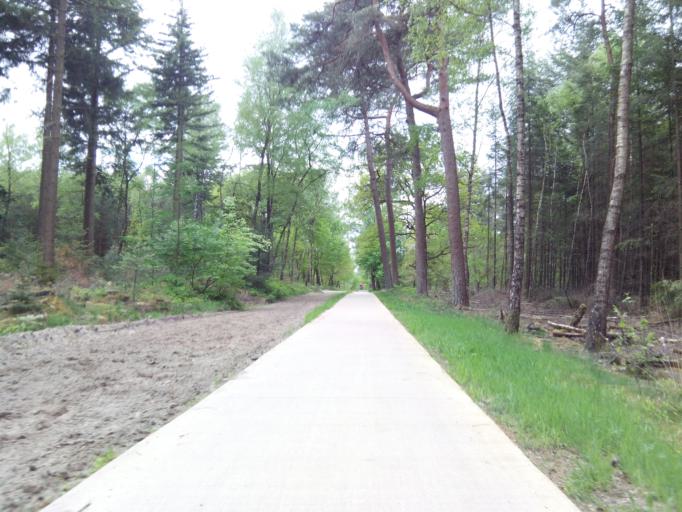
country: NL
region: Gelderland
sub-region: Gemeente Ede
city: Wekerom
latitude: 52.0761
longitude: 5.7312
